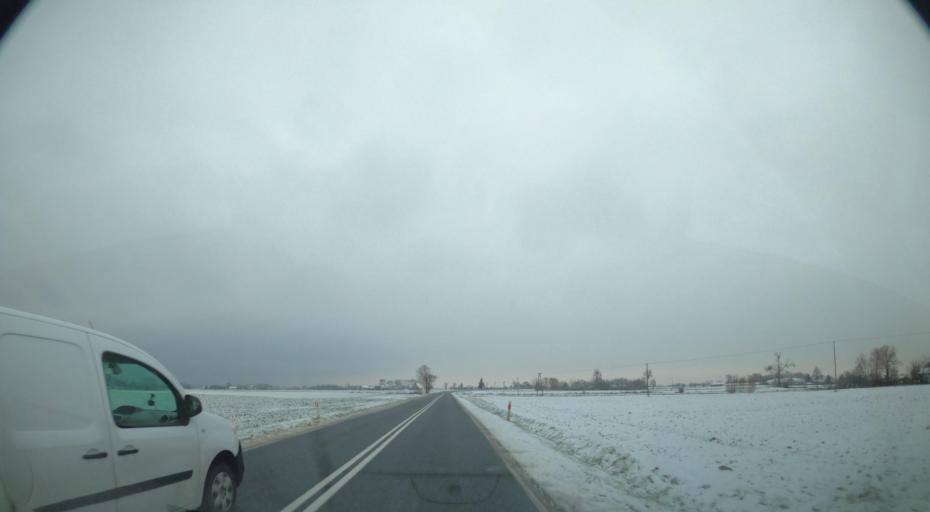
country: PL
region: Masovian Voivodeship
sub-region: Powiat plocki
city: Nowy Duninow
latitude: 52.6188
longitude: 19.4533
